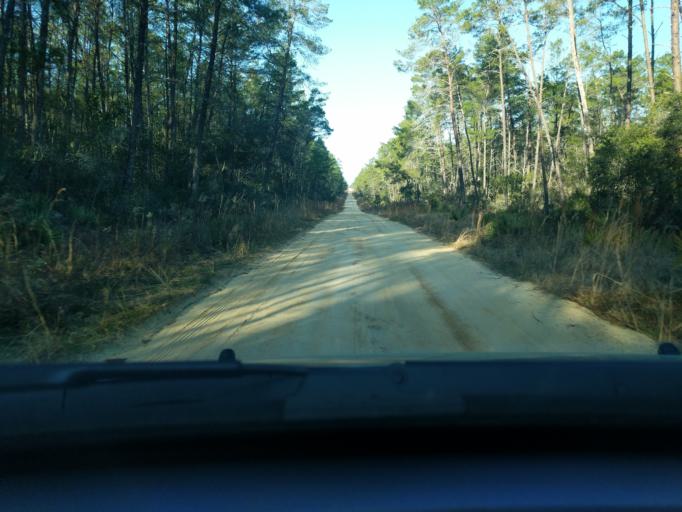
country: US
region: Florida
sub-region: Marion County
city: Silver Springs Shores
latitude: 29.2263
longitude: -81.7964
